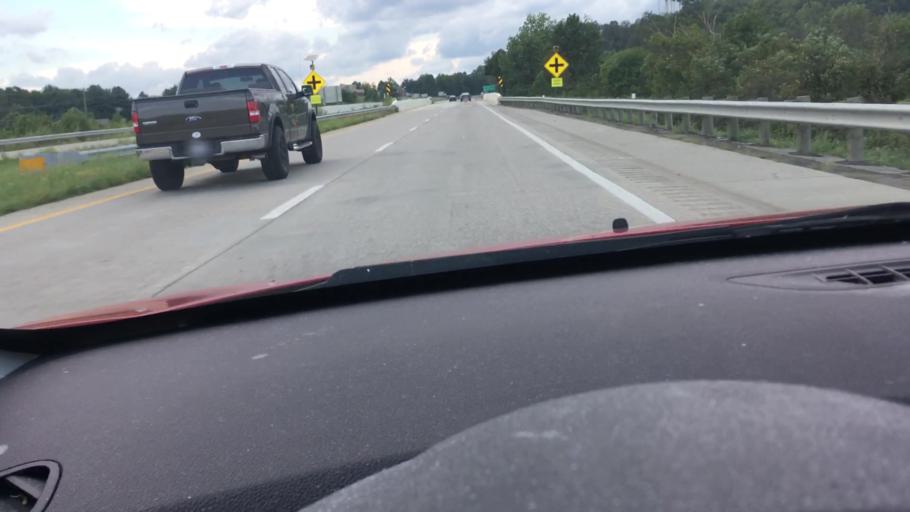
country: US
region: Ohio
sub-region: Athens County
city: The Plains
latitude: 39.3661
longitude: -82.1151
